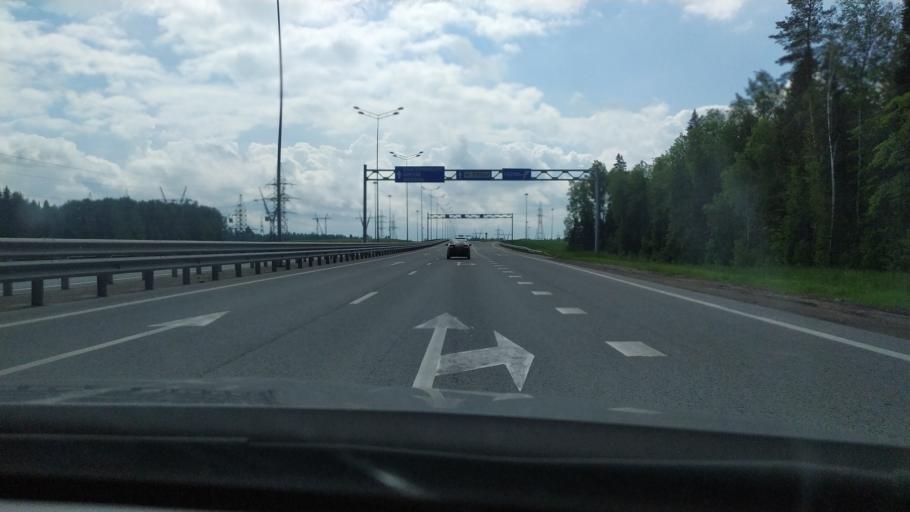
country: RU
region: Perm
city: Novyye Lyady
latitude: 58.0509
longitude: 56.4290
